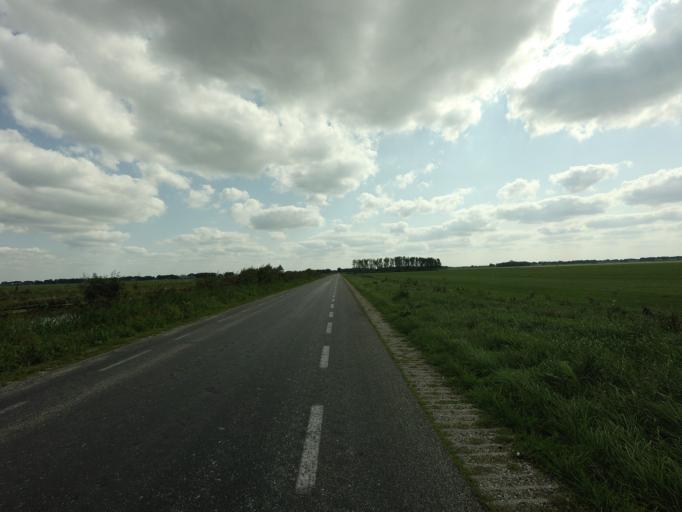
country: NL
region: Drenthe
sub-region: Gemeente Westerveld
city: Dwingeloo
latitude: 52.8831
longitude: 6.4236
